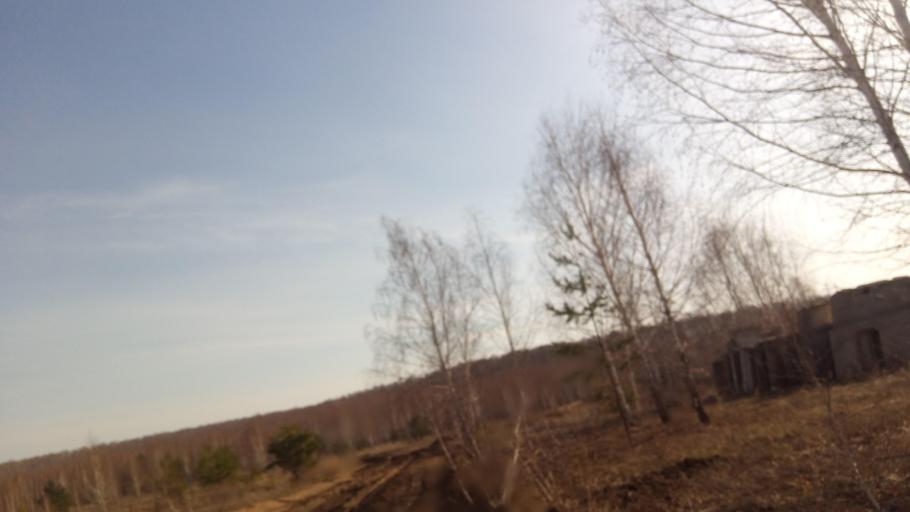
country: RU
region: Chelyabinsk
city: Sargazy
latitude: 55.1213
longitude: 61.2426
